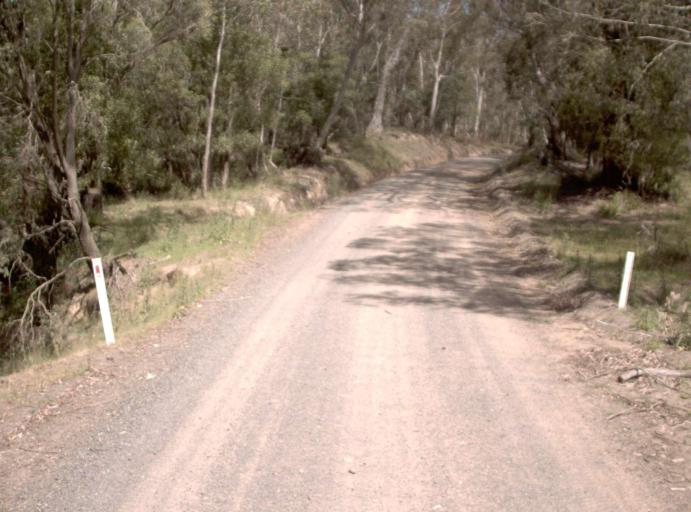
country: AU
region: New South Wales
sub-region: Bombala
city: Bombala
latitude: -37.1648
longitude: 148.6790
